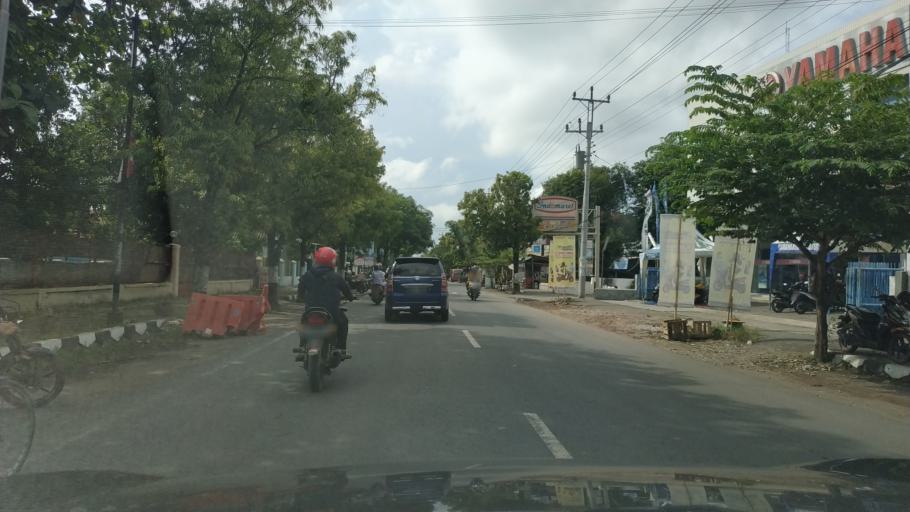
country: ID
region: Central Java
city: Pemalang
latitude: -6.9000
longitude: 109.3833
